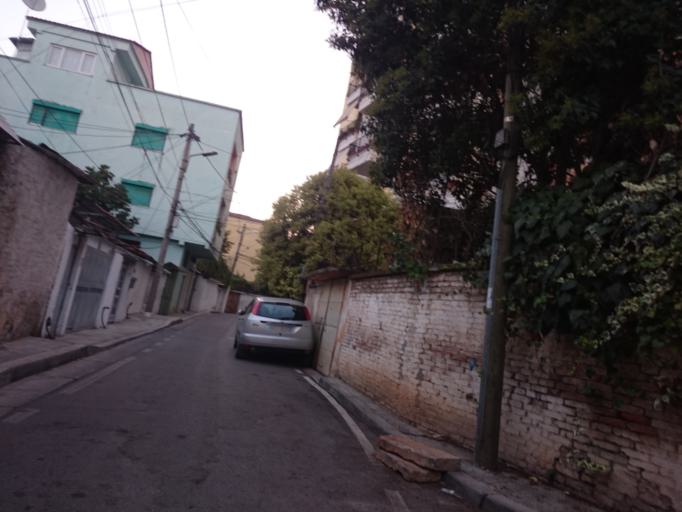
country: AL
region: Tirane
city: Tirana
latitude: 41.3300
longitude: 19.8087
